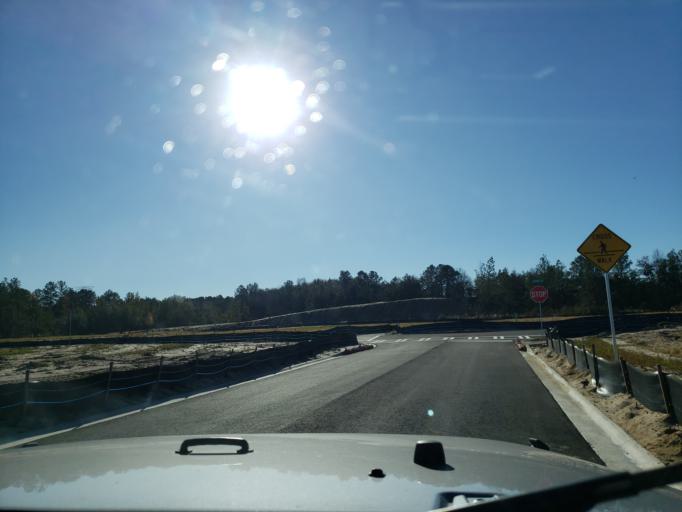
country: US
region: Georgia
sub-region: Chatham County
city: Bloomingdale
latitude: 32.0697
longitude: -81.3386
